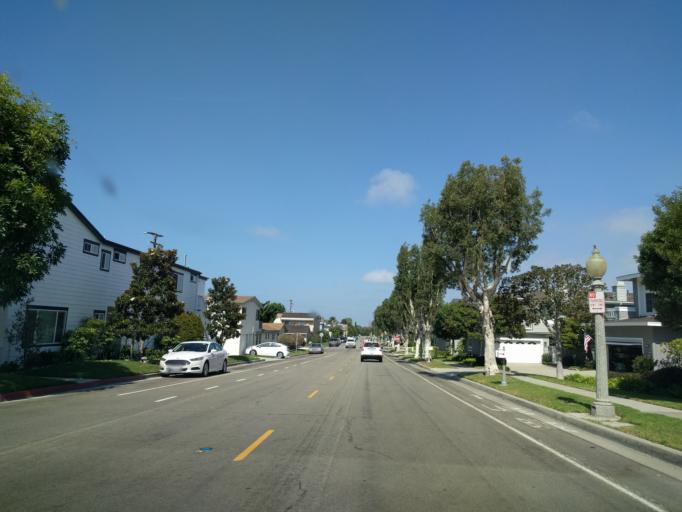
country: US
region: California
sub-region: Orange County
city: San Joaquin Hills
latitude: 33.5976
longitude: -117.8644
